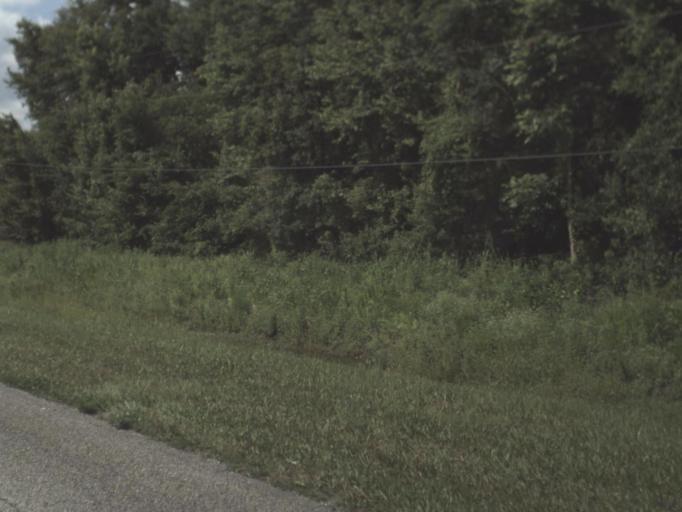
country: US
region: Florida
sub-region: Alachua County
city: Waldo
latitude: 29.7139
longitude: -82.1387
